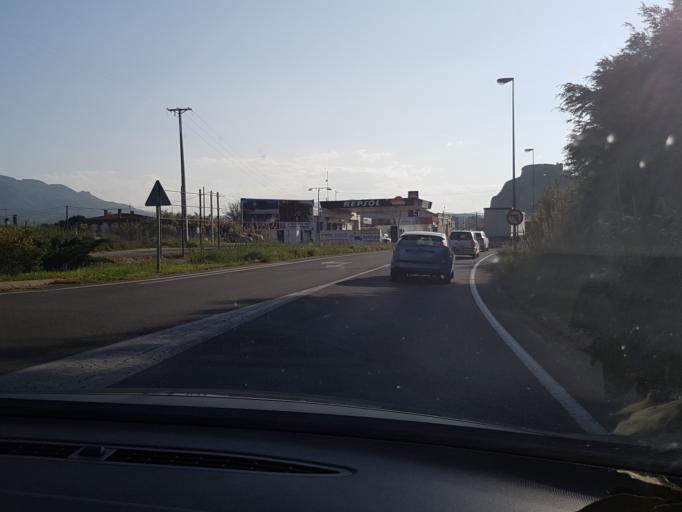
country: ES
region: La Rioja
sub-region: Provincia de La Rioja
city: Arnedo
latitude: 42.2305
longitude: -2.0842
